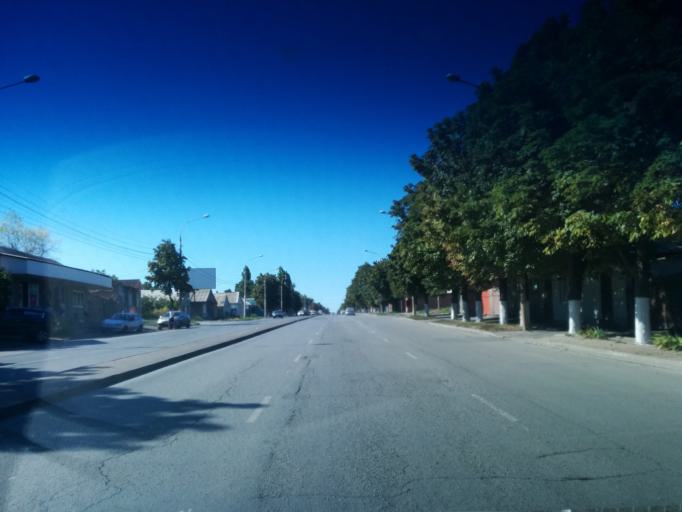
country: RU
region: Rostov
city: Shakhty
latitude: 47.7013
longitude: 40.2313
